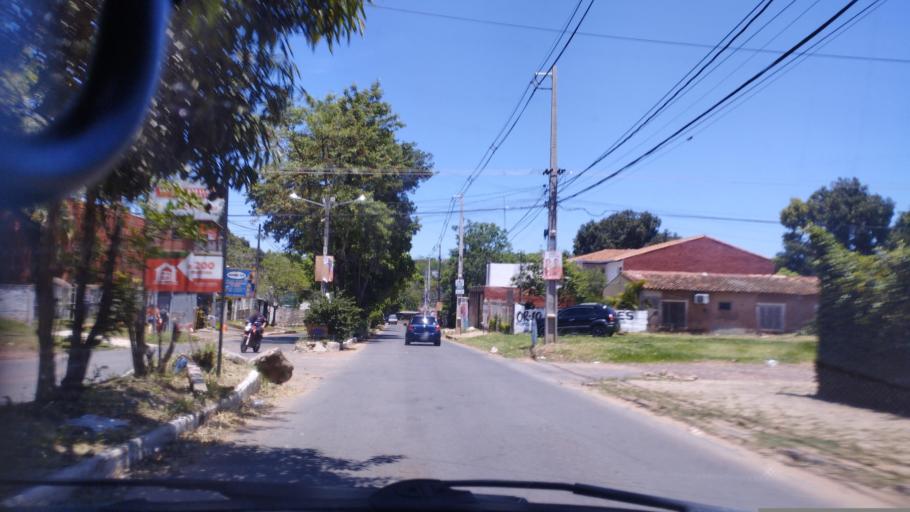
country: PY
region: Central
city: Nemby
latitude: -25.3773
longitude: -57.5437
